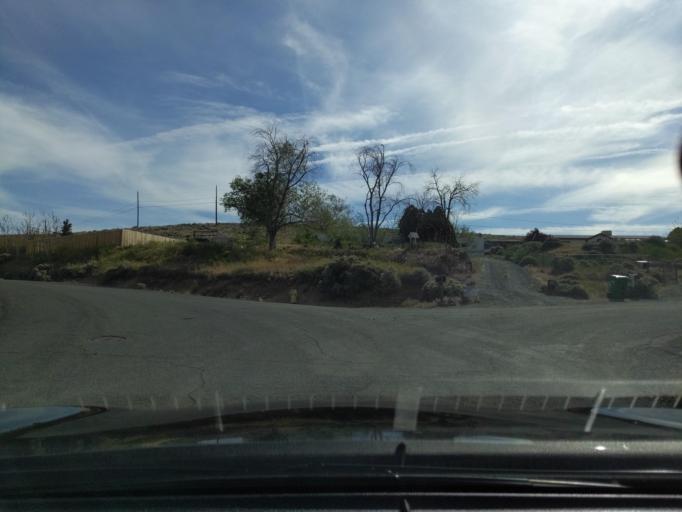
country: US
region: Nevada
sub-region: Washoe County
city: Sun Valley
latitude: 39.5741
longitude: -119.7839
